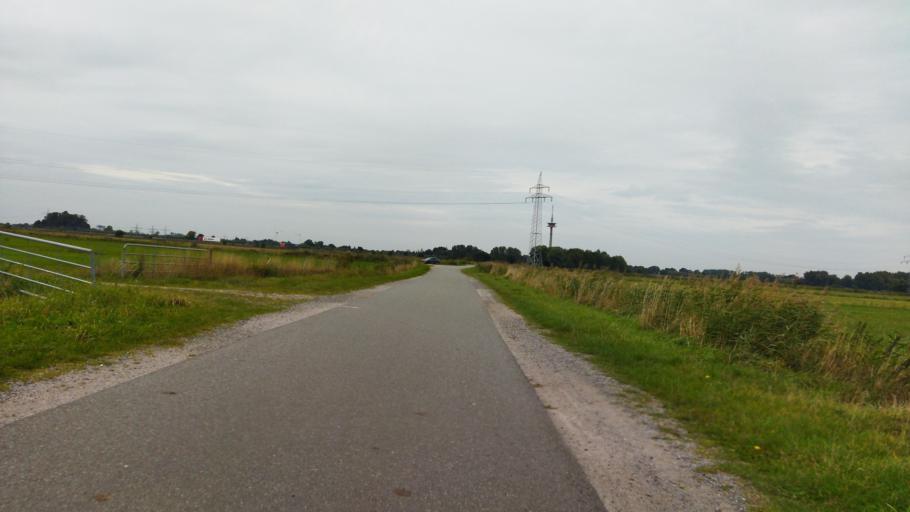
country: DE
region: Lower Saxony
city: Leer
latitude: 53.2492
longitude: 7.4386
